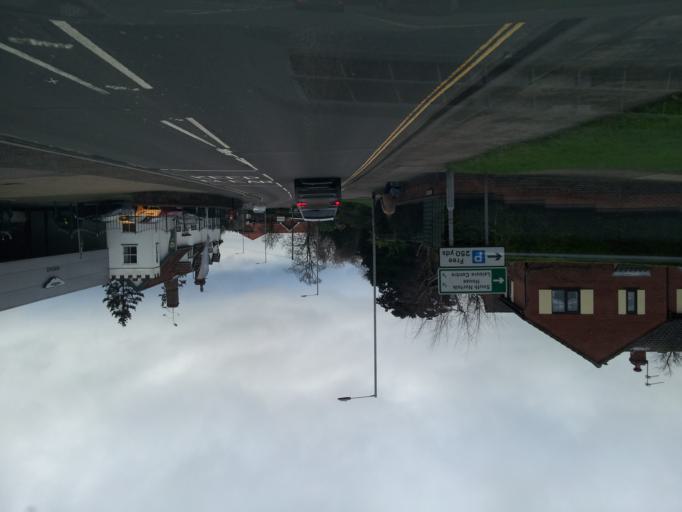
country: GB
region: England
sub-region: Norfolk
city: Long Stratton
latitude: 52.4856
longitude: 1.2337
